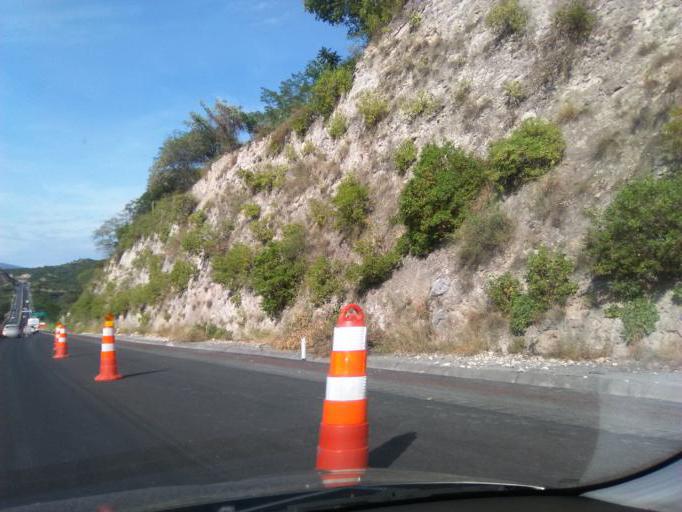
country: MX
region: Morelos
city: Tilzapotla
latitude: 18.4478
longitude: -99.1739
